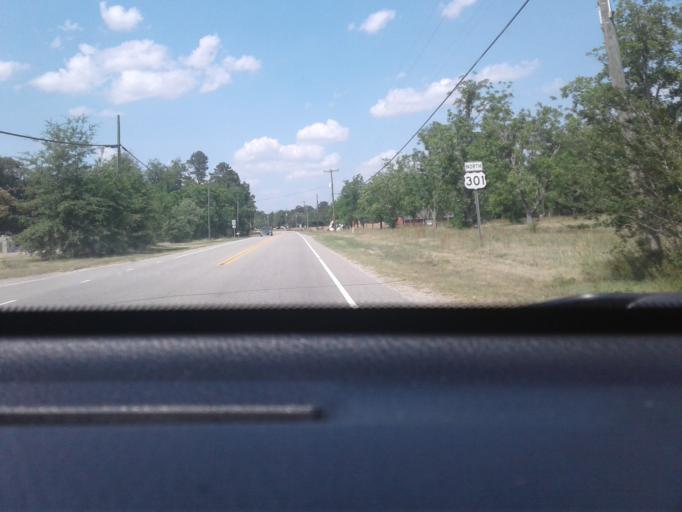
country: US
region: North Carolina
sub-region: Cumberland County
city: Eastover
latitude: 35.1611
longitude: -78.7292
